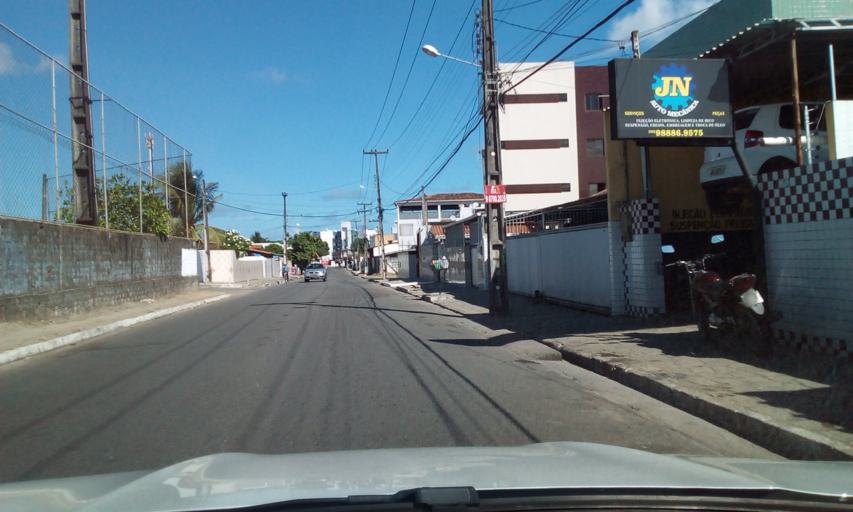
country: BR
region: Paraiba
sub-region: Joao Pessoa
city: Joao Pessoa
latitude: -7.1809
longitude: -34.8639
